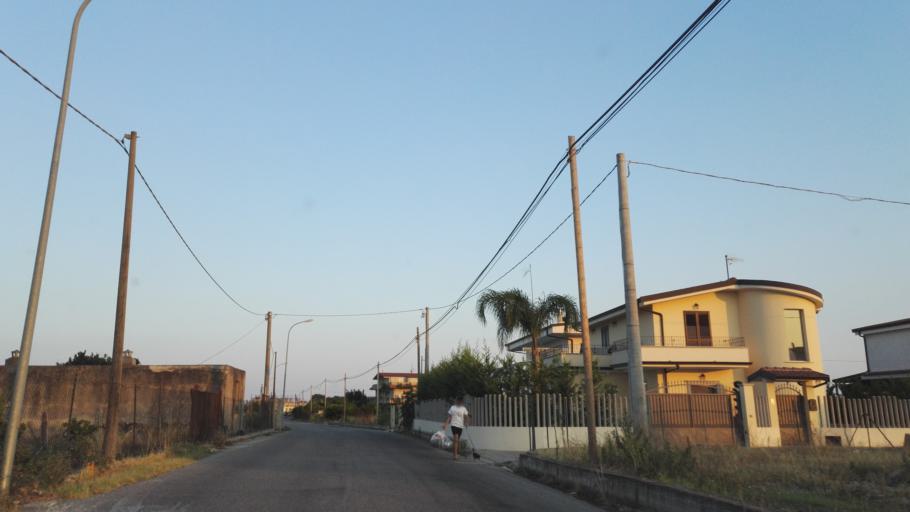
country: IT
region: Calabria
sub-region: Provincia di Reggio Calabria
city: Caulonia Marina
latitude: 38.3536
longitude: 16.4710
